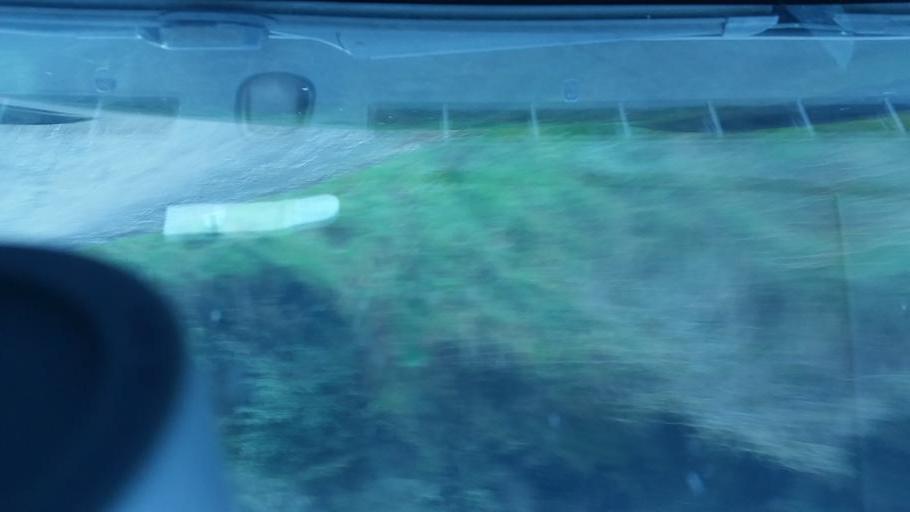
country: NZ
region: Marlborough
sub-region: Marlborough District
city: Blenheim
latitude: -41.5894
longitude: 174.0890
